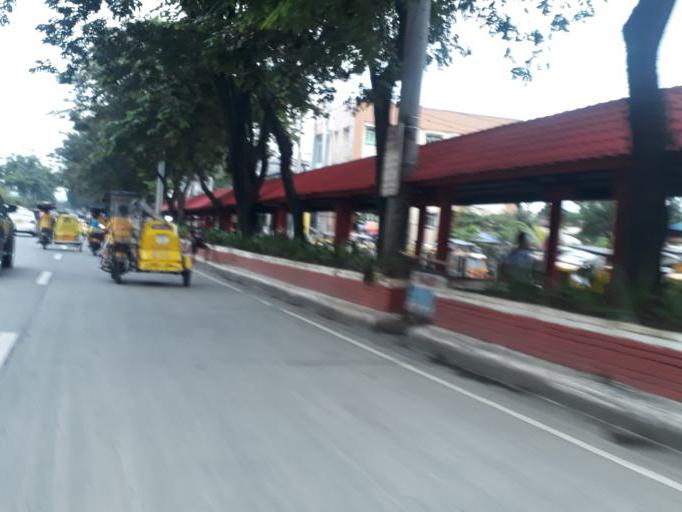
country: PH
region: Calabarzon
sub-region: Province of Rizal
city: San Mateo
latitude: 14.6867
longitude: 121.0877
